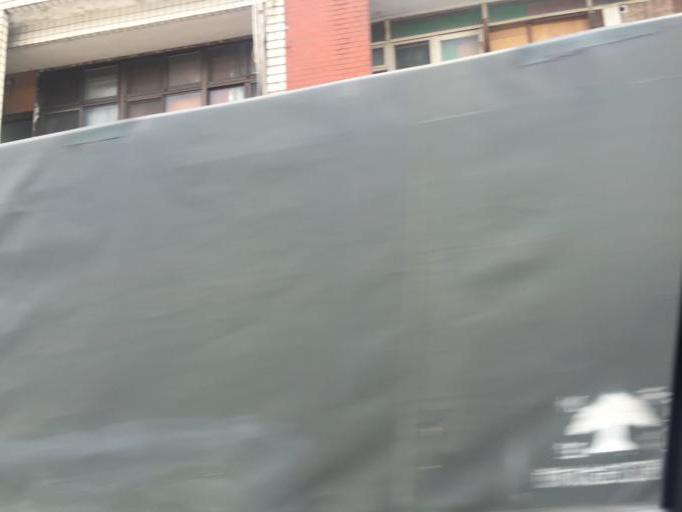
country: TW
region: Taiwan
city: Daxi
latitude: 24.8577
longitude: 121.2021
